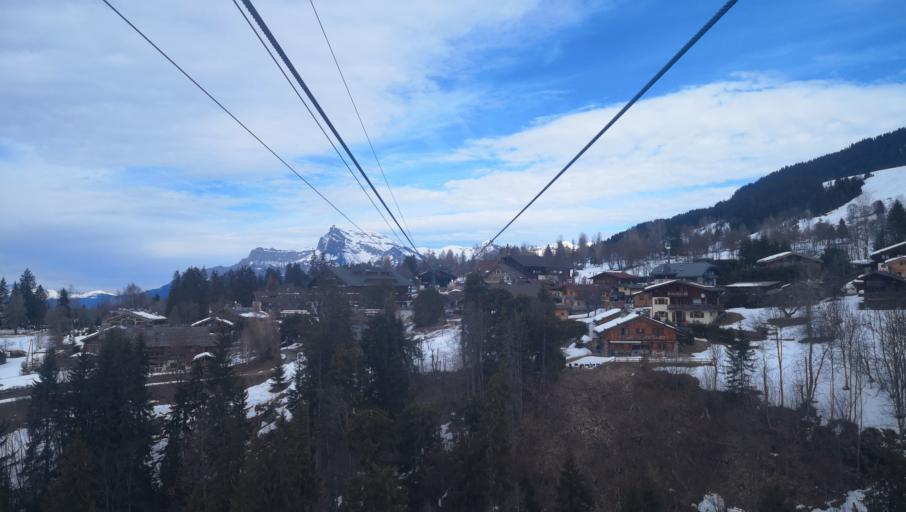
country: FR
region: Rhone-Alpes
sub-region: Departement de la Haute-Savoie
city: Megeve
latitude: 45.8513
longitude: 6.6301
